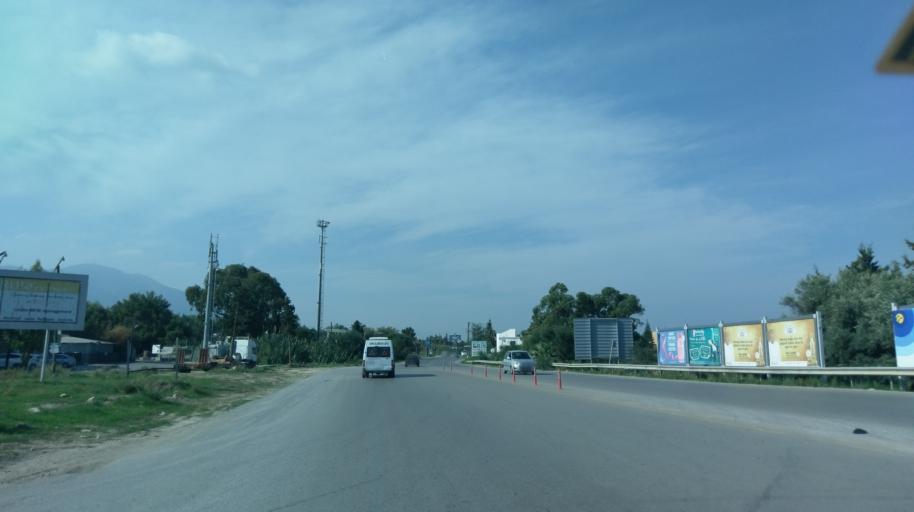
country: CY
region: Keryneia
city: Lapithos
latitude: 35.3429
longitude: 33.2454
